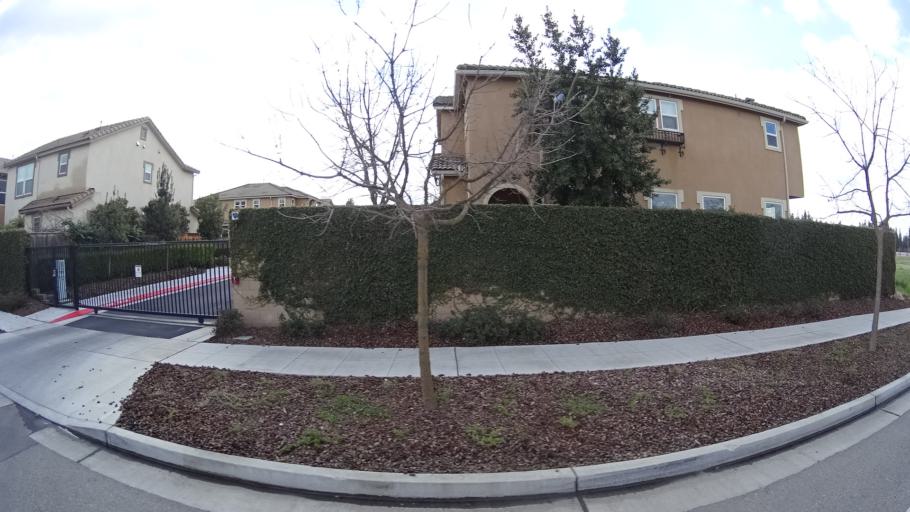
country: US
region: California
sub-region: Fresno County
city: Fresno
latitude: 36.8388
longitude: -119.8521
